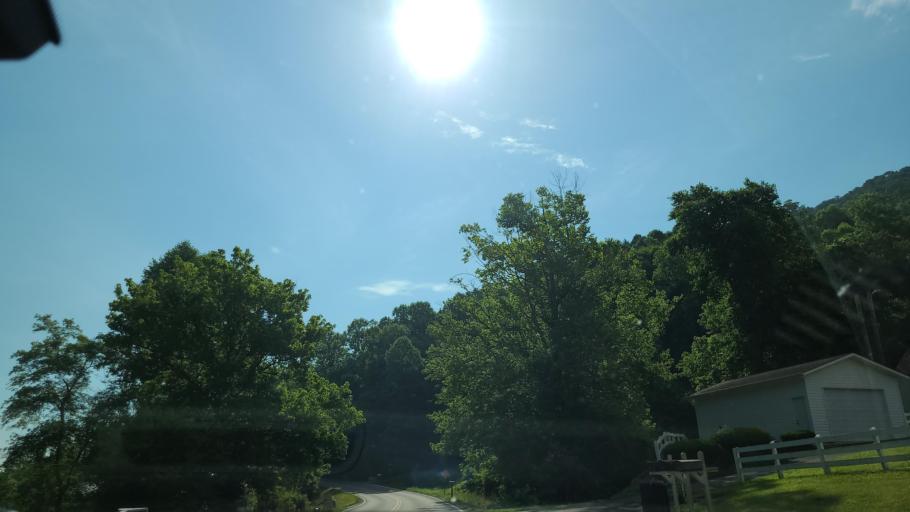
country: US
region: Kentucky
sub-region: Bell County
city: Pineville
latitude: 36.7095
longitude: -83.8278
